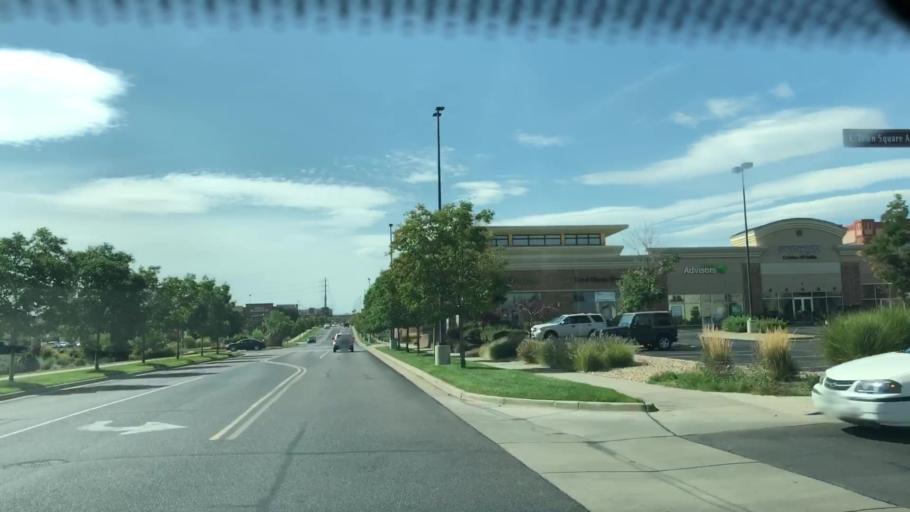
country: US
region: Colorado
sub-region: Douglas County
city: Parker
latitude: 39.6055
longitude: -104.7074
